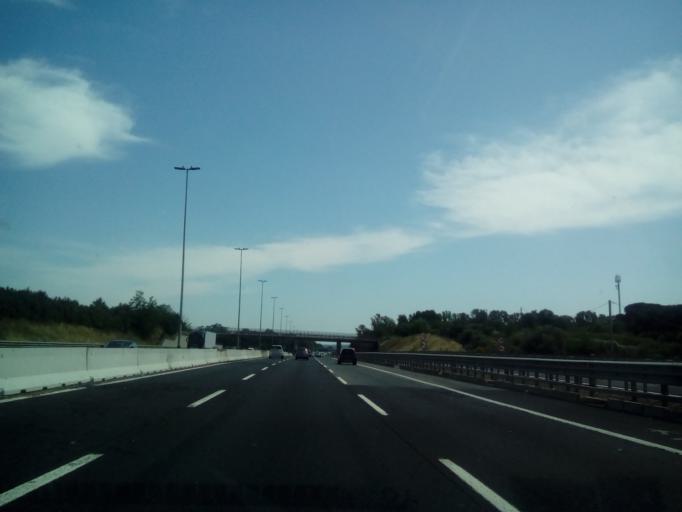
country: IT
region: Latium
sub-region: Citta metropolitana di Roma Capitale
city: La Massimina-Casal Lumbroso
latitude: 41.8432
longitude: 12.3826
